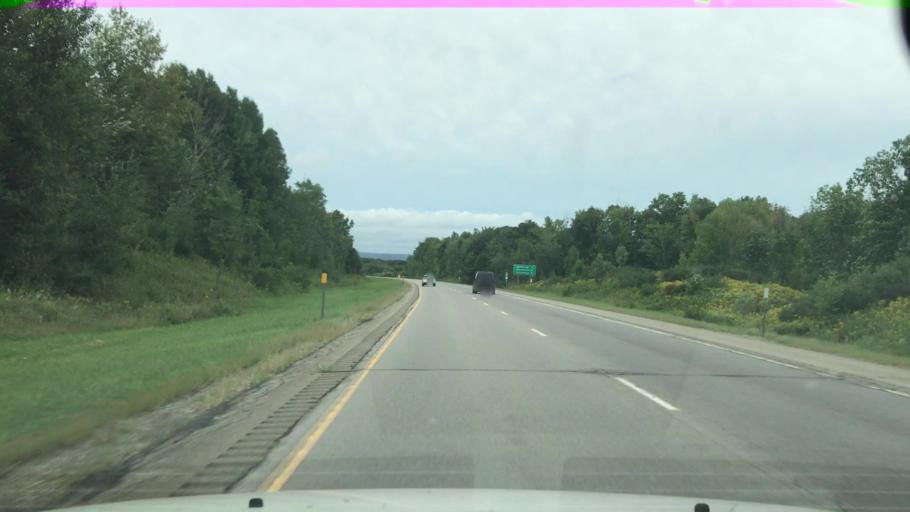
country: US
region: New York
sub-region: Erie County
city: Springville
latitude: 42.5446
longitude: -78.7108
